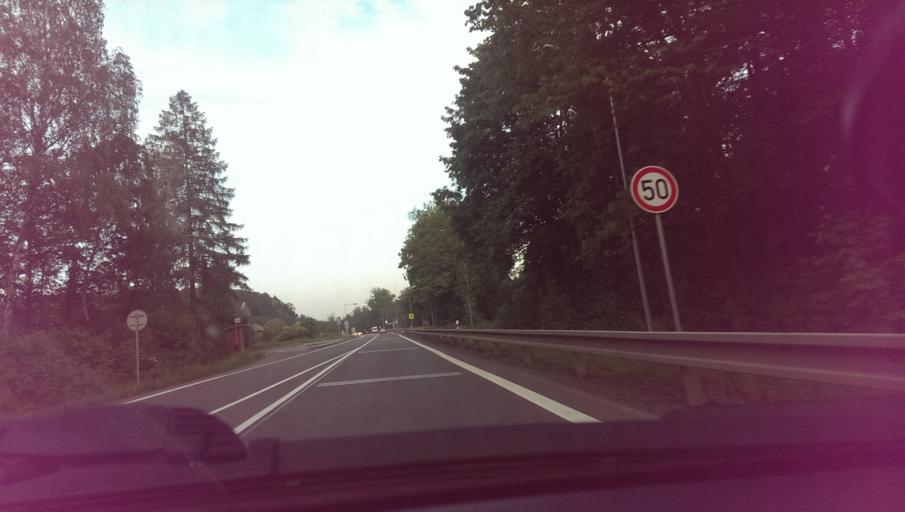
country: CZ
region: Zlin
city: Valasske Mezirici
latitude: 49.4757
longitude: 18.0049
